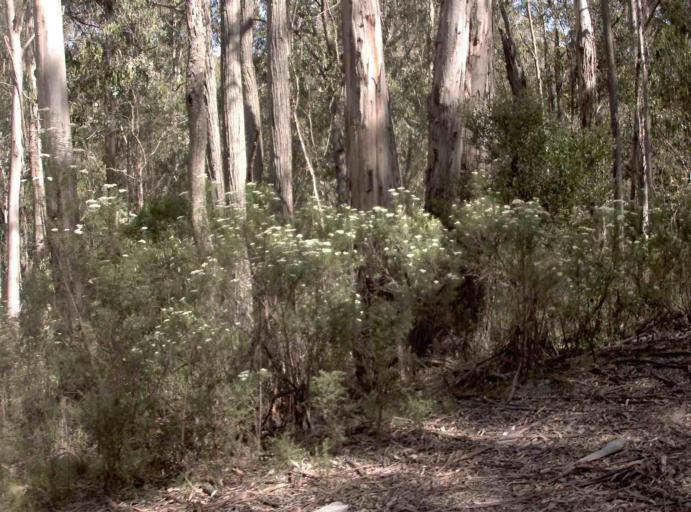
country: AU
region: New South Wales
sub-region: Bombala
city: Bombala
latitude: -37.2876
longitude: 148.7149
